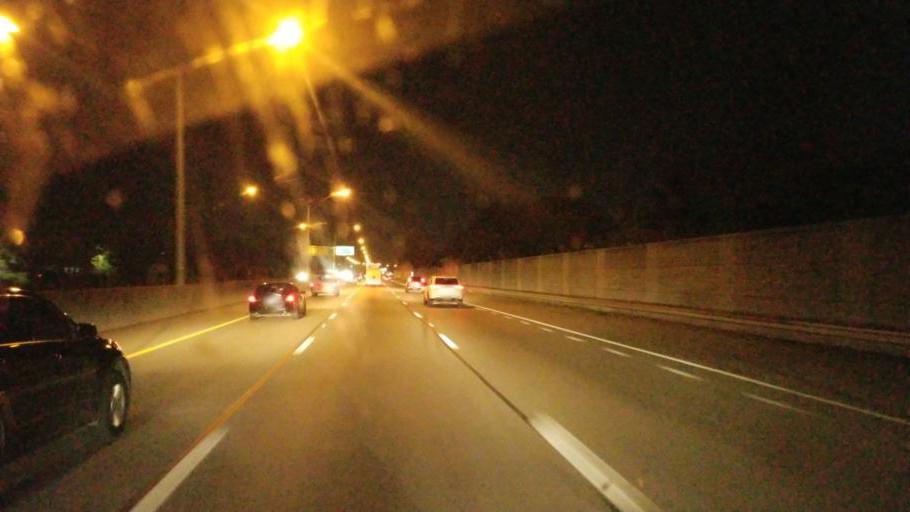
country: US
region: Ohio
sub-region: Franklin County
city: Worthington
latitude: 40.0518
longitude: -82.9977
